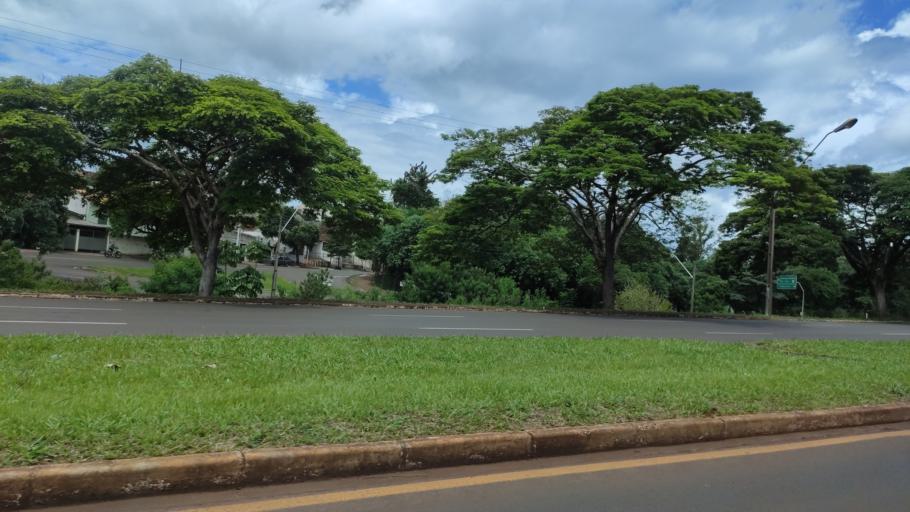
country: BR
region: Parana
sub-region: Londrina
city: Londrina
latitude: -23.3387
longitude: -51.1449
